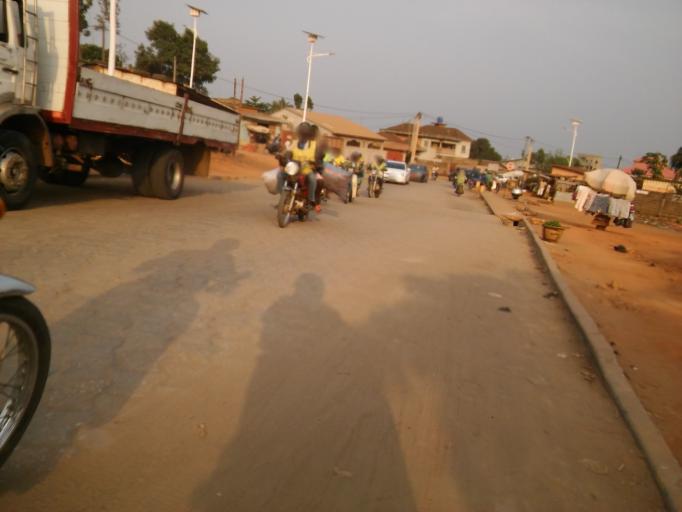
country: BJ
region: Atlantique
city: Abomey-Calavi
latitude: 6.4034
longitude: 2.3374
